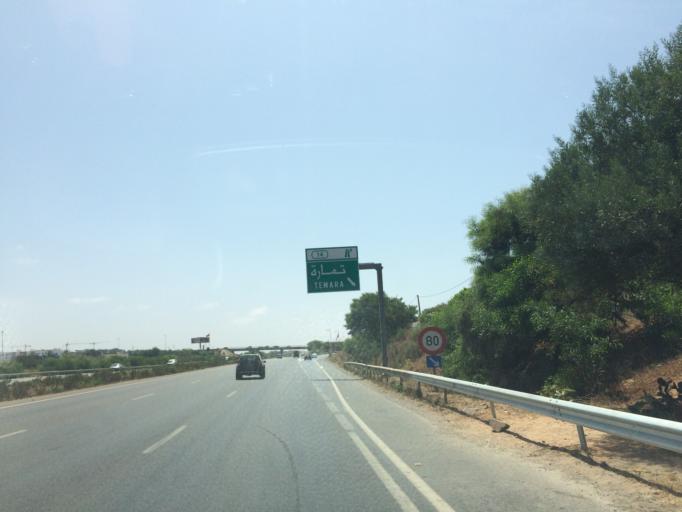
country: MA
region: Rabat-Sale-Zemmour-Zaer
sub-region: Skhirate-Temara
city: Temara
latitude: 33.9360
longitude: -6.9333
